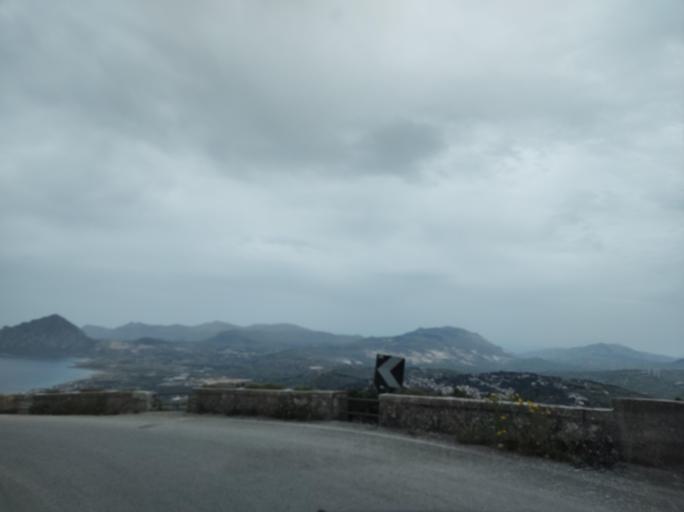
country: IT
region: Sicily
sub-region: Trapani
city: Erice
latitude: 38.0408
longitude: 12.5936
